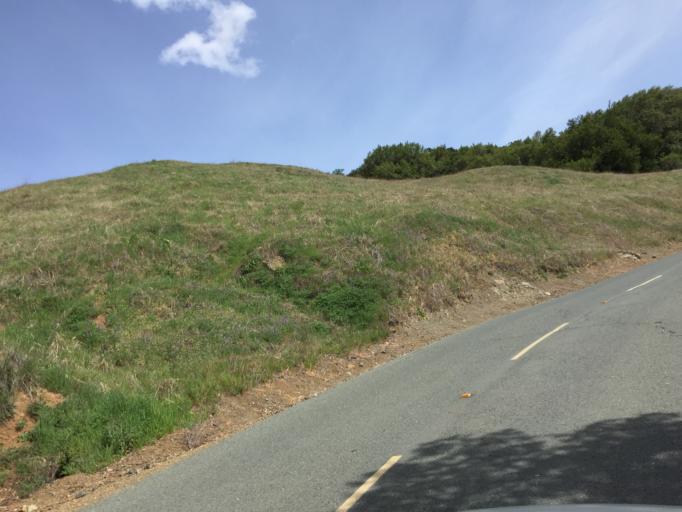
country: US
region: California
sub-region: Contra Costa County
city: Diablo
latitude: 37.8714
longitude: -121.9402
